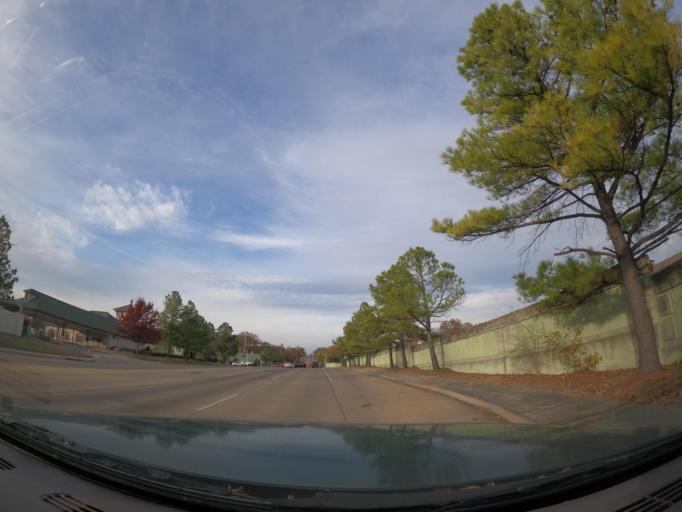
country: US
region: Oklahoma
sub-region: Tulsa County
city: Jenks
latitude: 36.0599
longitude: -95.9399
